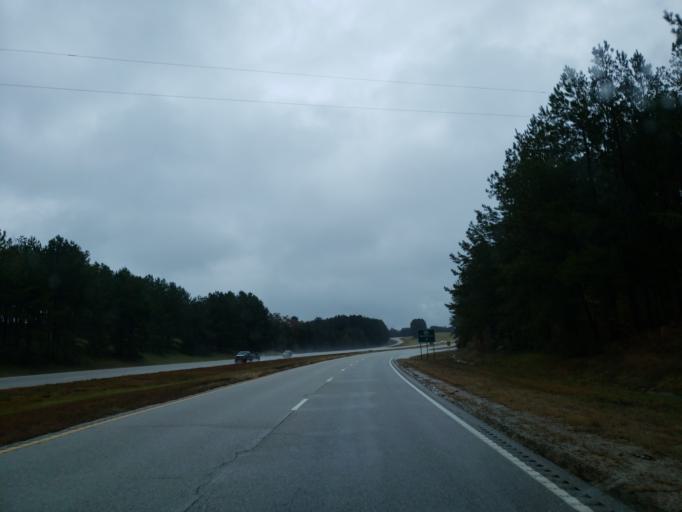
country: US
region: Mississippi
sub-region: Lauderdale County
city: Meridian
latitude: 32.2970
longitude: -88.6947
